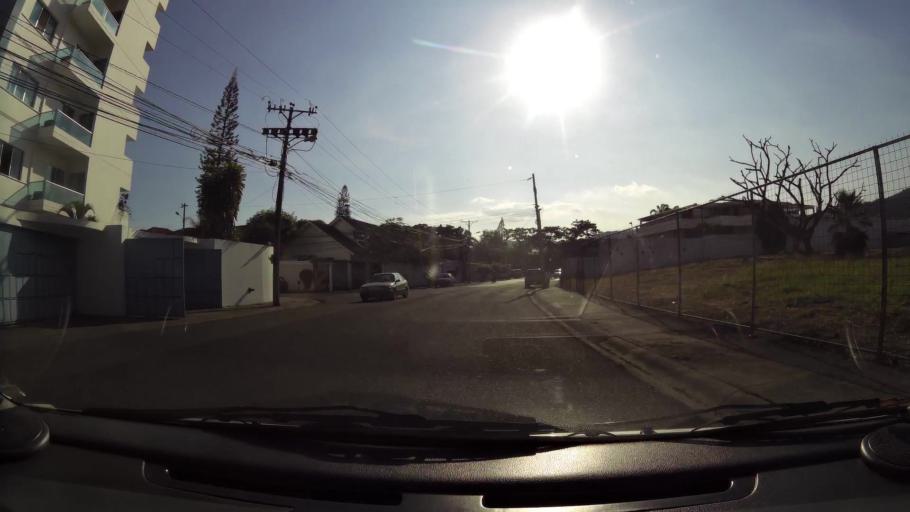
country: EC
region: Guayas
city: Santa Lucia
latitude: -2.1879
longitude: -79.9664
